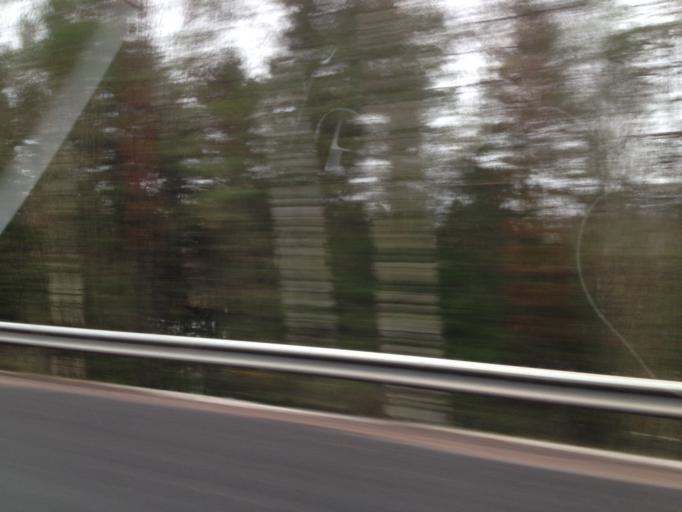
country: FI
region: Uusimaa
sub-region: Raaseporin
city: Ekenaes
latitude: 59.9924
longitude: 23.5009
